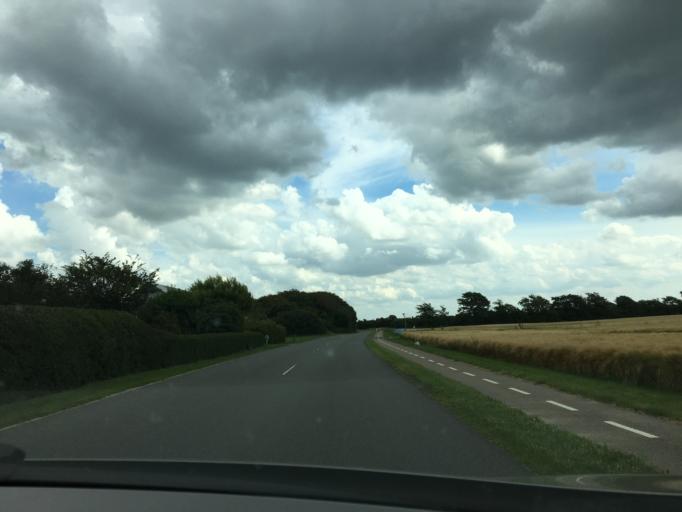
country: DK
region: Central Jutland
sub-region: Ringkobing-Skjern Kommune
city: Skjern
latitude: 55.9514
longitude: 8.4060
